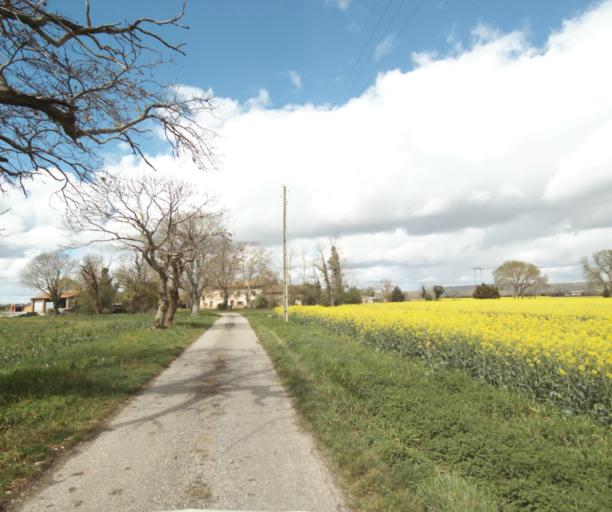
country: FR
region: Midi-Pyrenees
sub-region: Departement de l'Ariege
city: Saverdun
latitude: 43.2637
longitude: 1.5950
